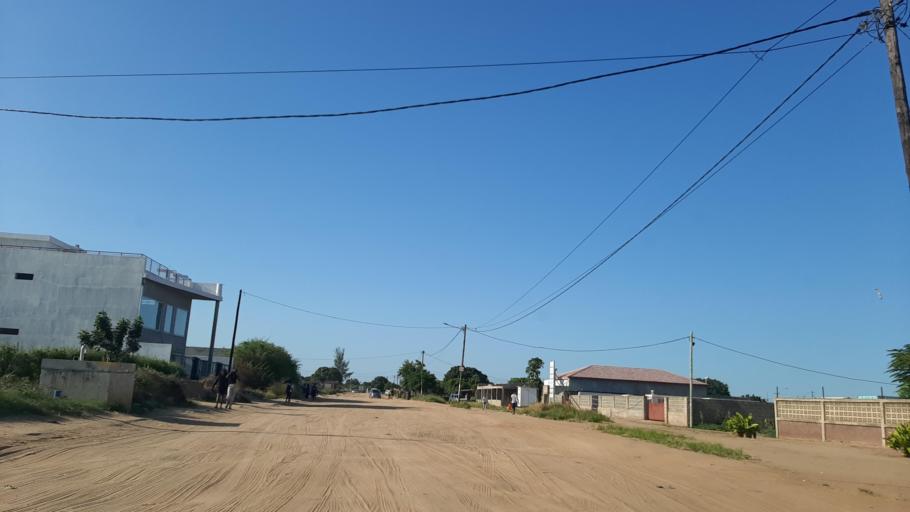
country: MZ
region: Maputo City
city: Maputo
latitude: -25.8068
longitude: 32.5466
